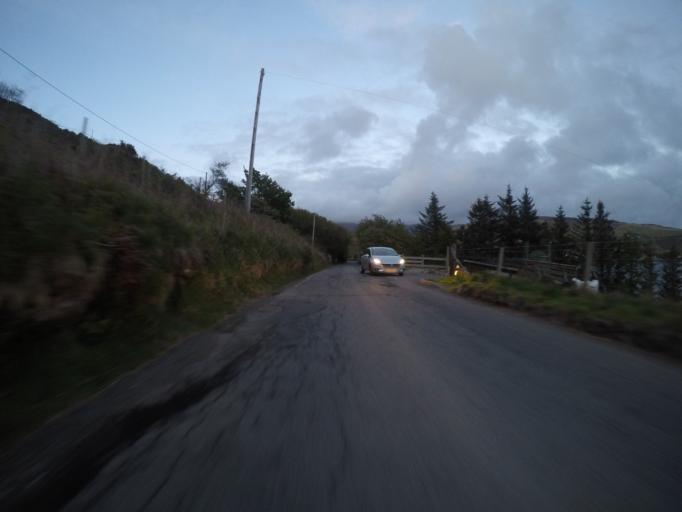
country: GB
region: Scotland
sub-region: Highland
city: Portree
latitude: 57.5921
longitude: -6.3689
